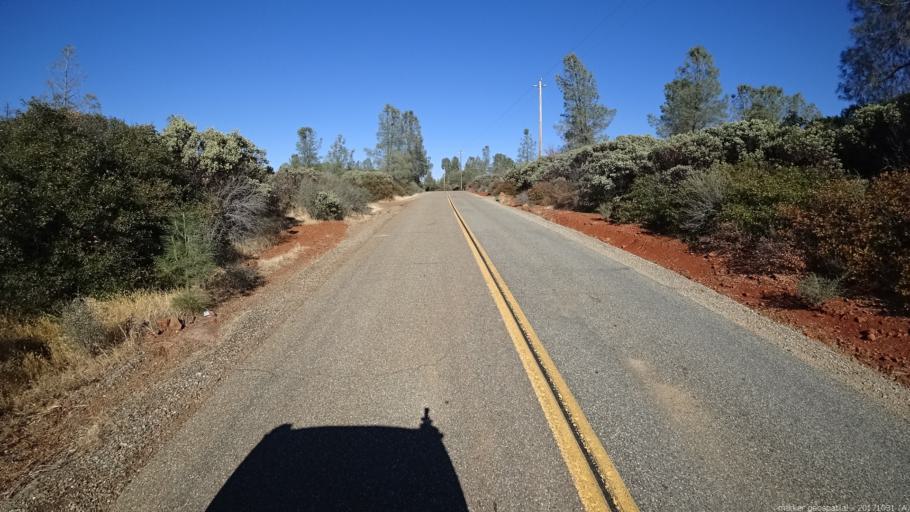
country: US
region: California
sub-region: Shasta County
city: Shingletown
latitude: 40.4944
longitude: -121.9977
